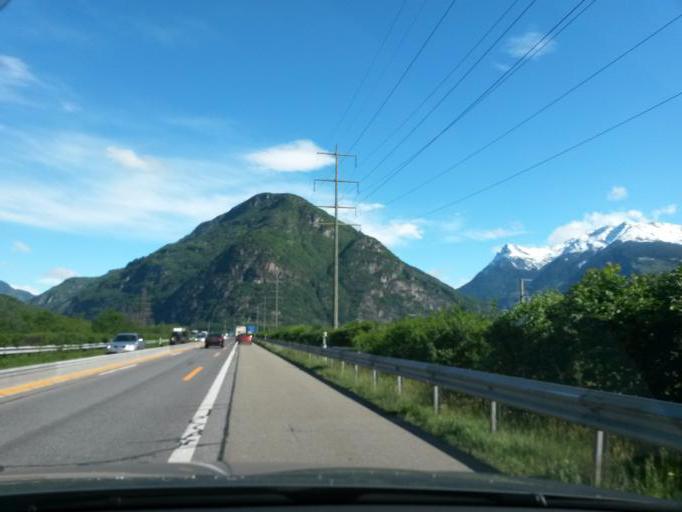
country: CH
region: Ticino
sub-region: Riviera District
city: Biasca
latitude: 46.3419
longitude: 8.9692
